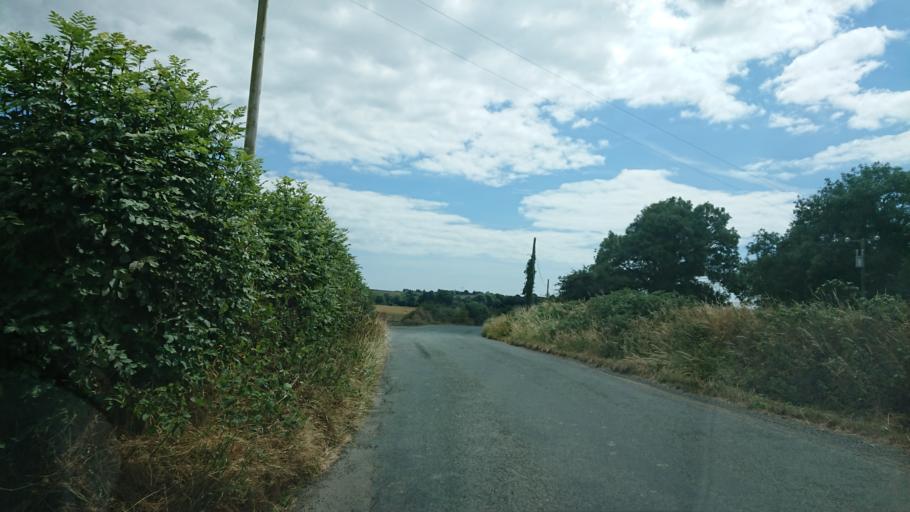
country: IE
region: Munster
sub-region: Waterford
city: Portlaw
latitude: 52.2173
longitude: -7.3320
